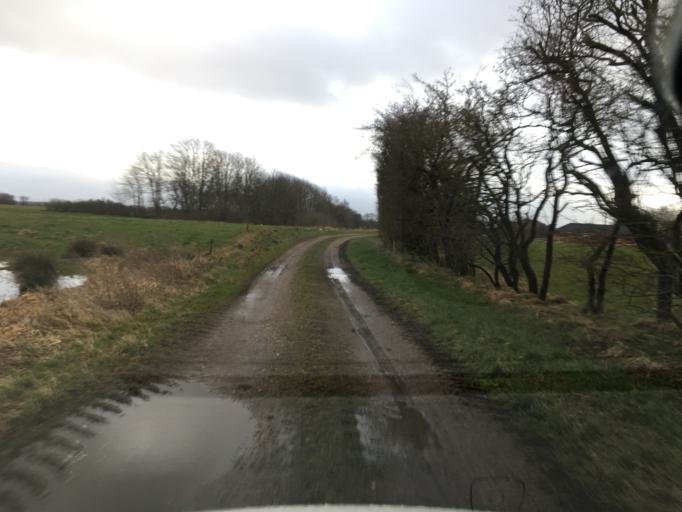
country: DE
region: Schleswig-Holstein
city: Boxlund
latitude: 54.9395
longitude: 9.1457
